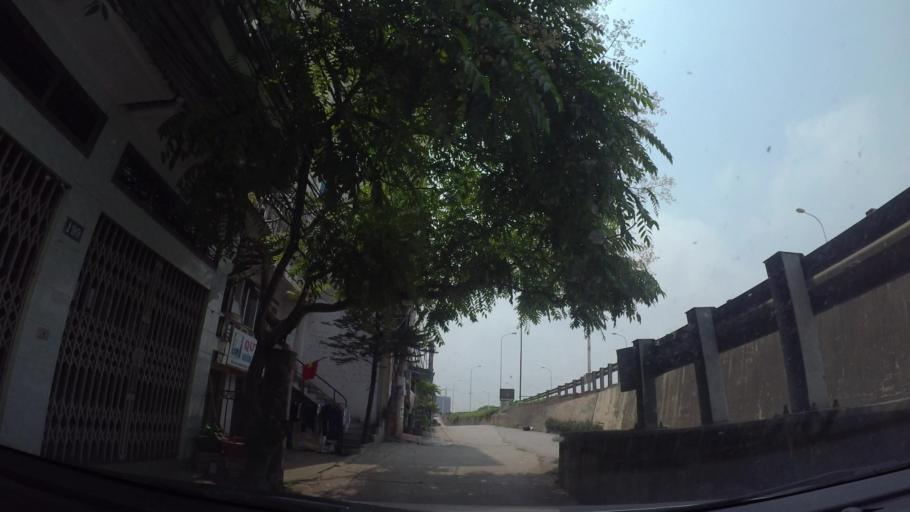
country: VN
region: Ha Noi
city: Tay Ho
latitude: 21.0897
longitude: 105.8052
